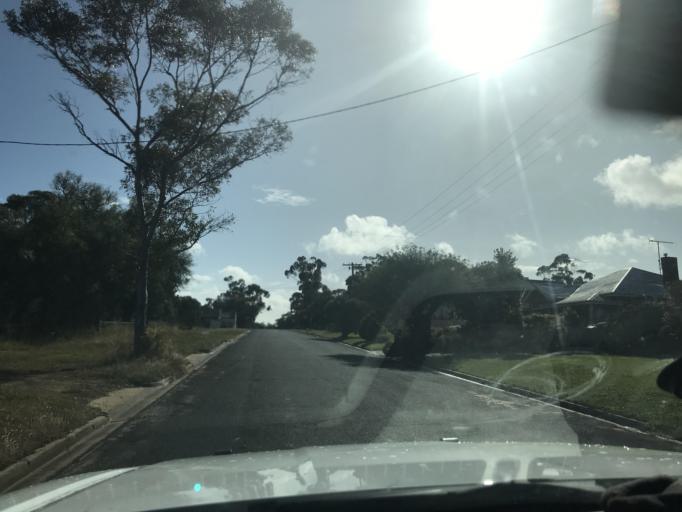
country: AU
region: Victoria
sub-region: Horsham
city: Horsham
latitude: -36.7194
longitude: 141.4739
